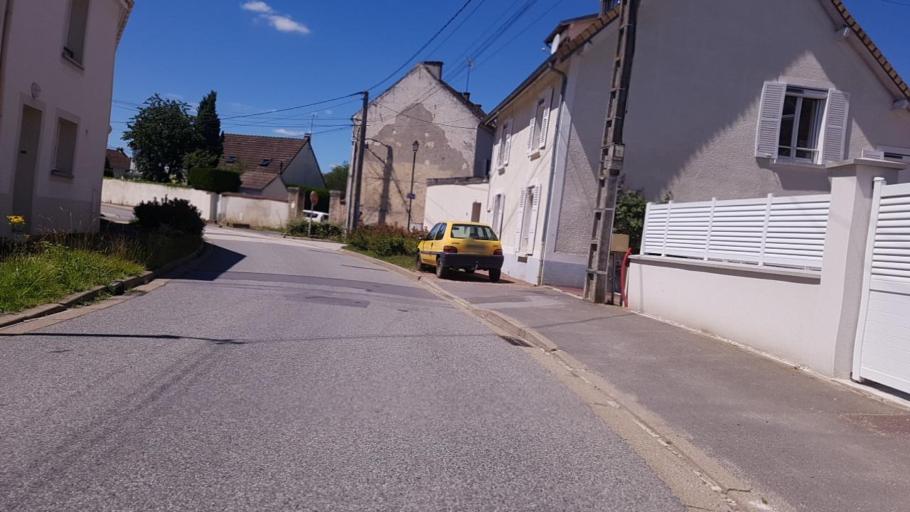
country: FR
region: Ile-de-France
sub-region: Departement de Seine-et-Marne
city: Sammeron
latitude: 48.9547
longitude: 3.0776
